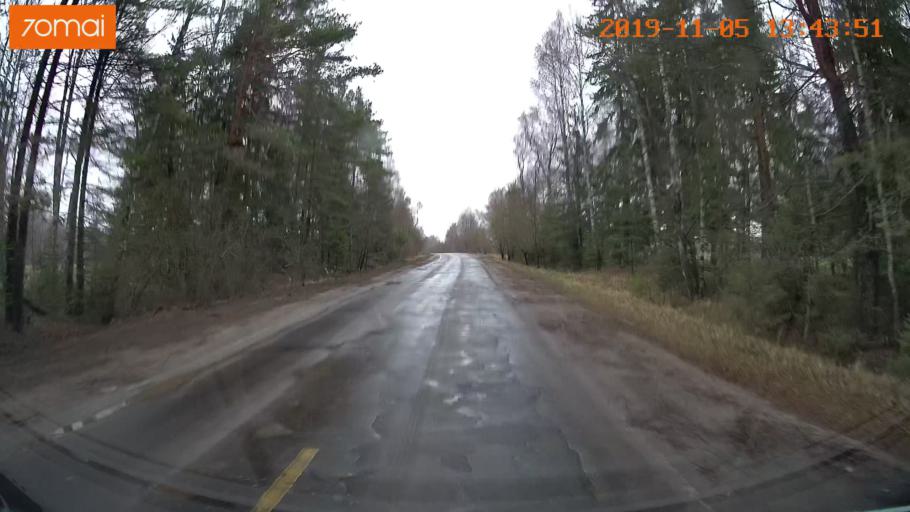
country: RU
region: Ivanovo
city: Shuya
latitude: 56.9765
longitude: 41.4062
